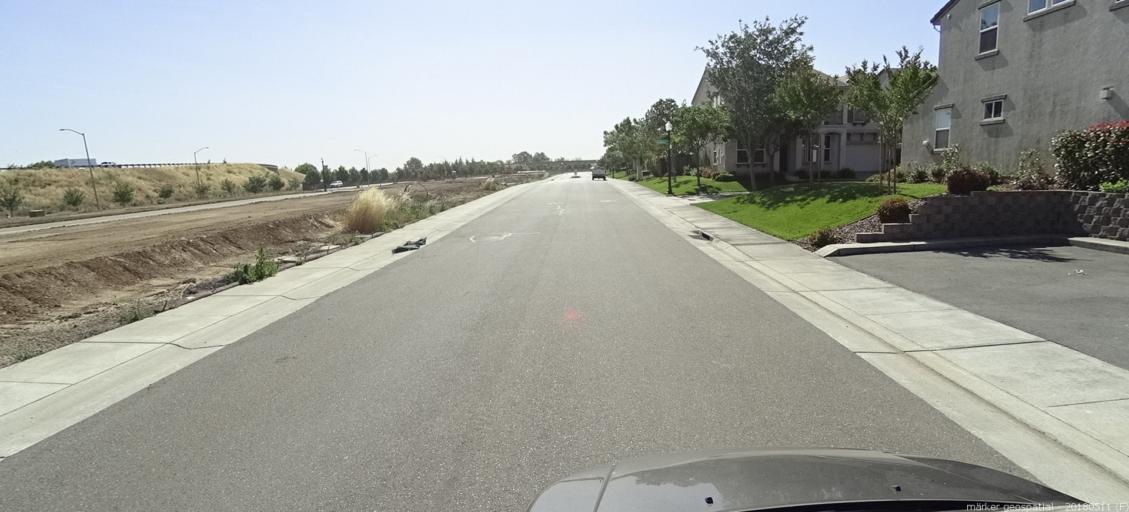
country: US
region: California
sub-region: Yolo County
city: West Sacramento
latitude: 38.6689
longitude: -121.5459
